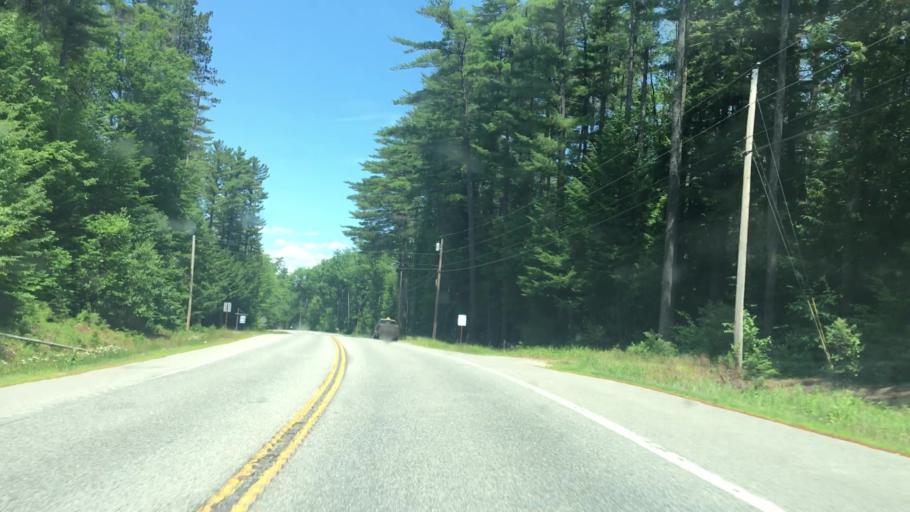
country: US
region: Maine
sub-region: Androscoggin County
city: Livermore Falls
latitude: 44.4314
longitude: -70.2123
